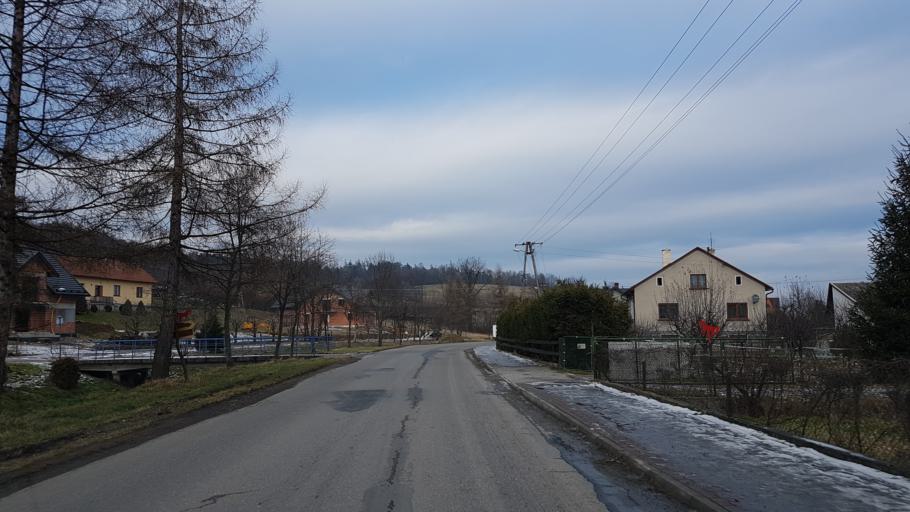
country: PL
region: Lesser Poland Voivodeship
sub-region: Powiat nowosadecki
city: Stary Sacz
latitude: 49.5446
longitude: 20.6170
